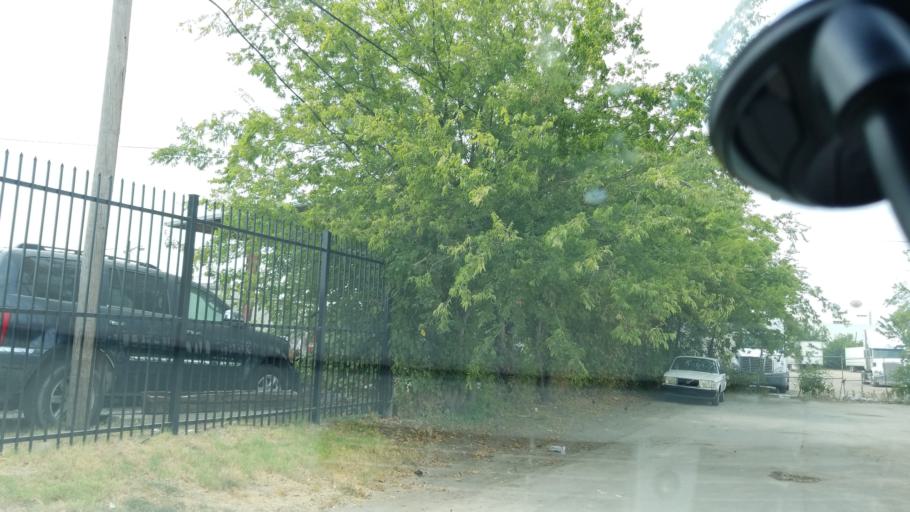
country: US
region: Texas
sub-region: Dallas County
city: Grand Prairie
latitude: 32.7474
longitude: -96.9822
